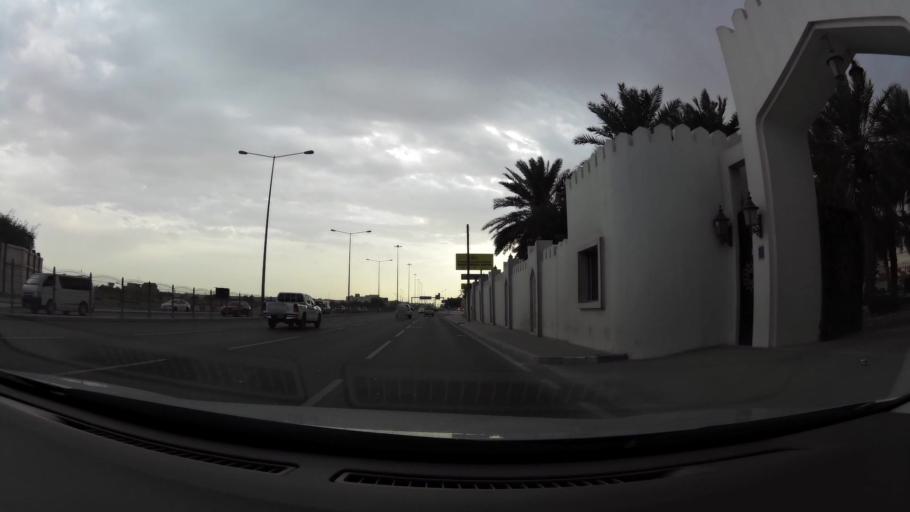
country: QA
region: Baladiyat ad Dawhah
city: Doha
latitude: 25.2675
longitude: 51.5028
